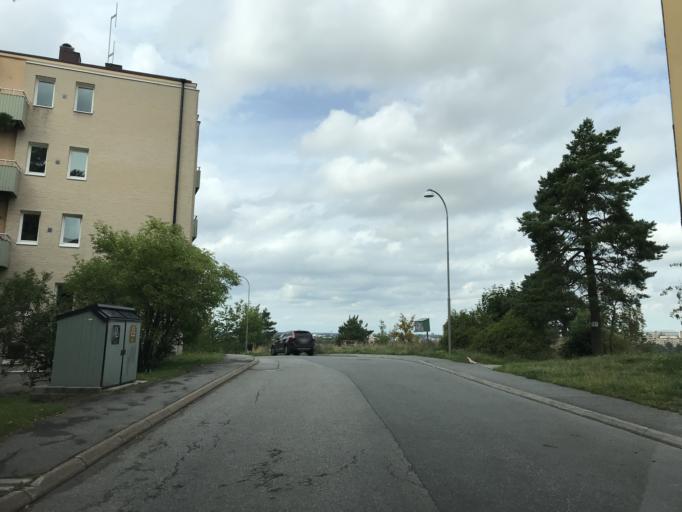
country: SE
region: Stockholm
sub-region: Sundbybergs Kommun
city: Sundbyberg
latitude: 59.3395
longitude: 17.9840
